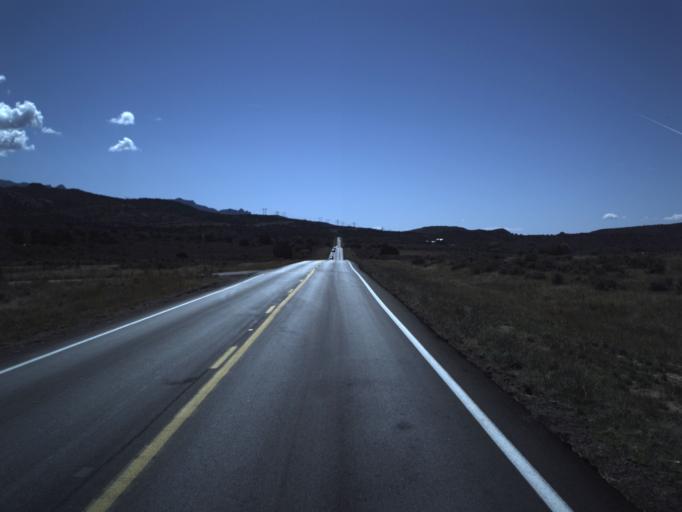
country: US
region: Utah
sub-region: Washington County
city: Enterprise
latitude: 37.4998
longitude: -113.6316
